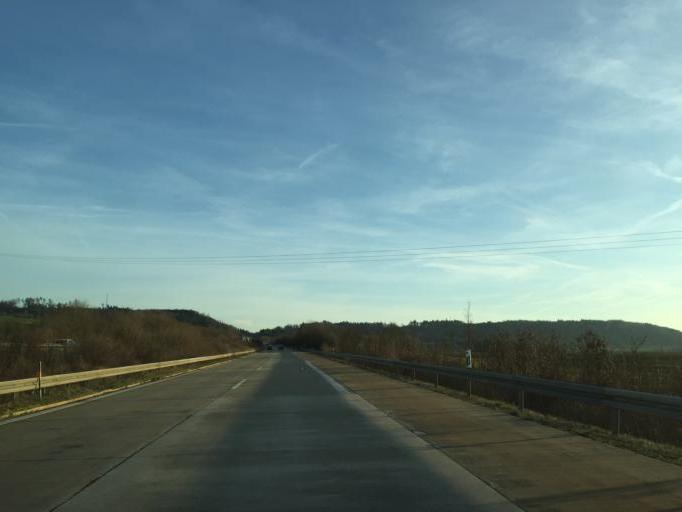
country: DE
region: Bavaria
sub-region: Regierungsbezirk Mittelfranken
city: Diebach
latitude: 49.2922
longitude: 10.2182
